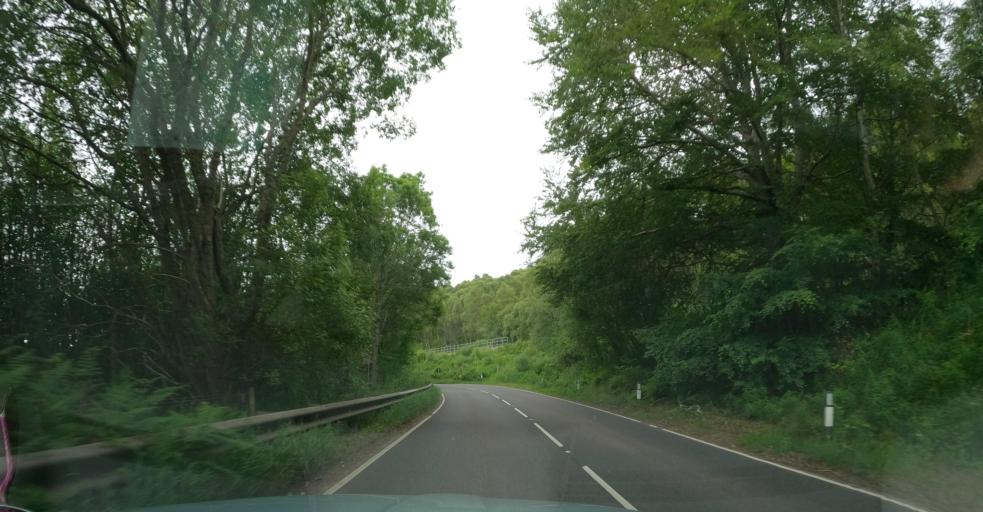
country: GB
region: Scotland
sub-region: Highland
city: Muir of Ord
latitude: 57.6195
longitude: -4.6945
